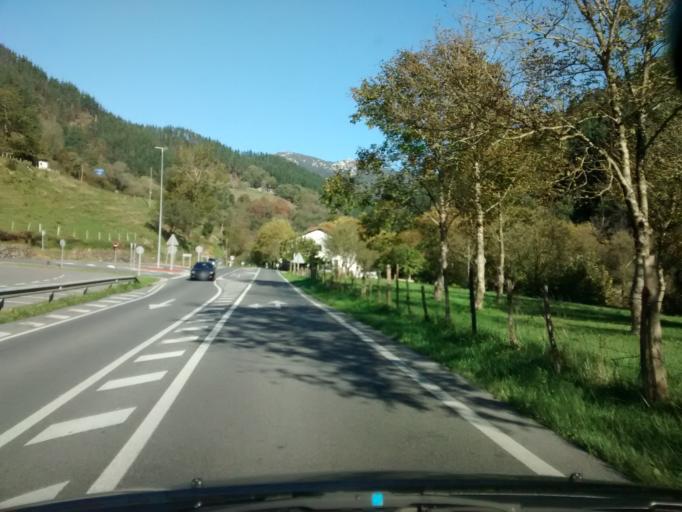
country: ES
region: Basque Country
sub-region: Provincia de Guipuzcoa
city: Mendaro
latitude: 43.2375
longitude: -2.3980
